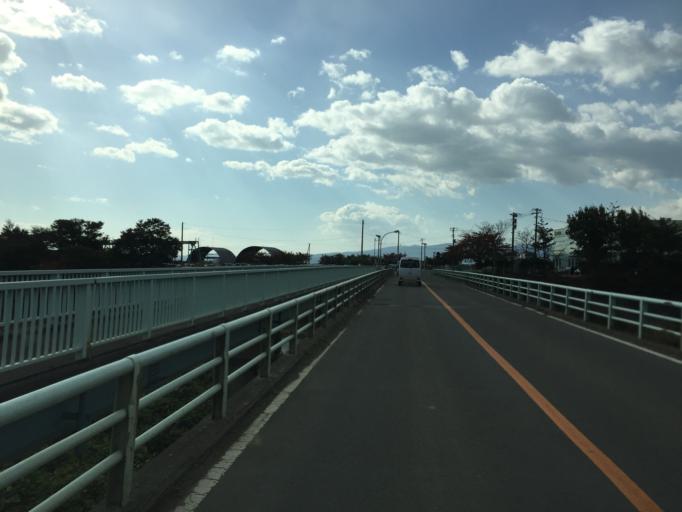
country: JP
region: Fukushima
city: Fukushima-shi
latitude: 37.7853
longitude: 140.3940
